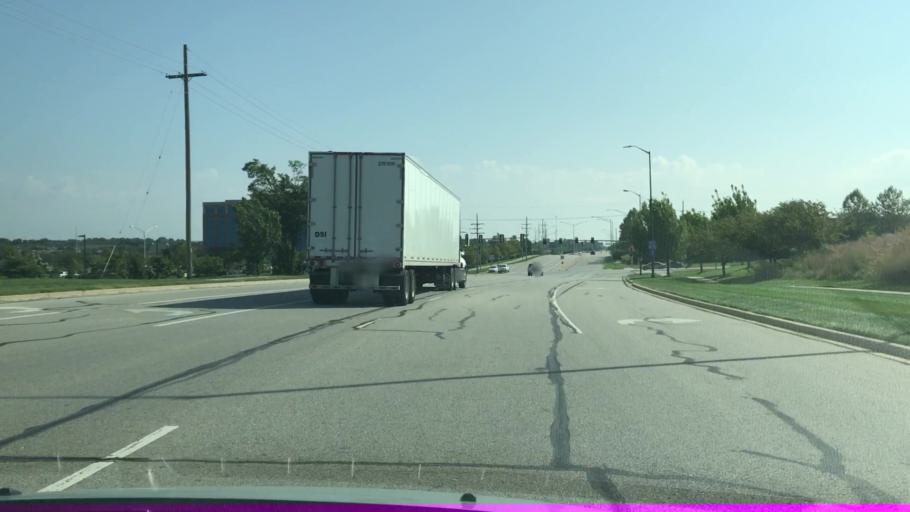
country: US
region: Kansas
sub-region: Johnson County
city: Lenexa
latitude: 38.9563
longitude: -94.7815
